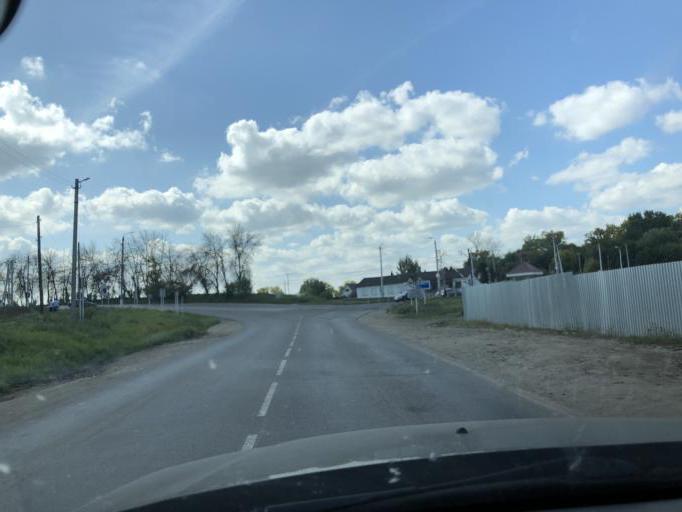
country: RU
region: Tula
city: Yasnogorsk
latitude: 54.4848
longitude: 37.6835
